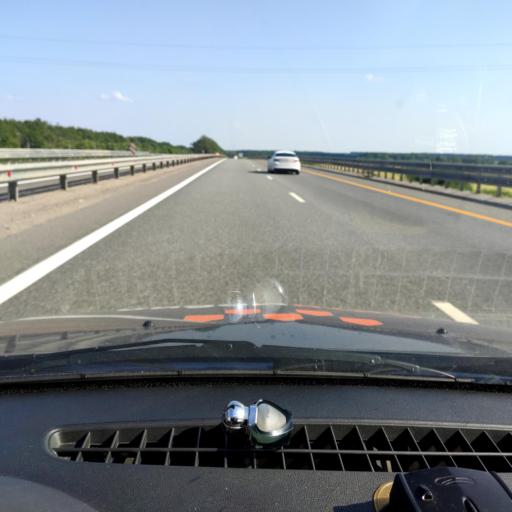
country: RU
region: Lipetsk
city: Zadonsk
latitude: 52.4602
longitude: 38.7744
